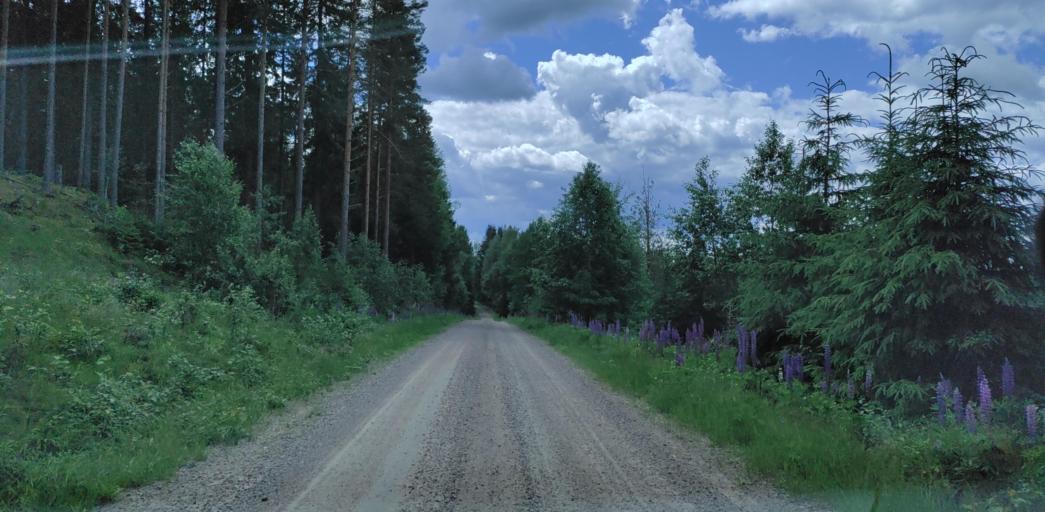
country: SE
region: Vaermland
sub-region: Hagfors Kommun
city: Ekshaerad
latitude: 60.0844
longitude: 13.3170
